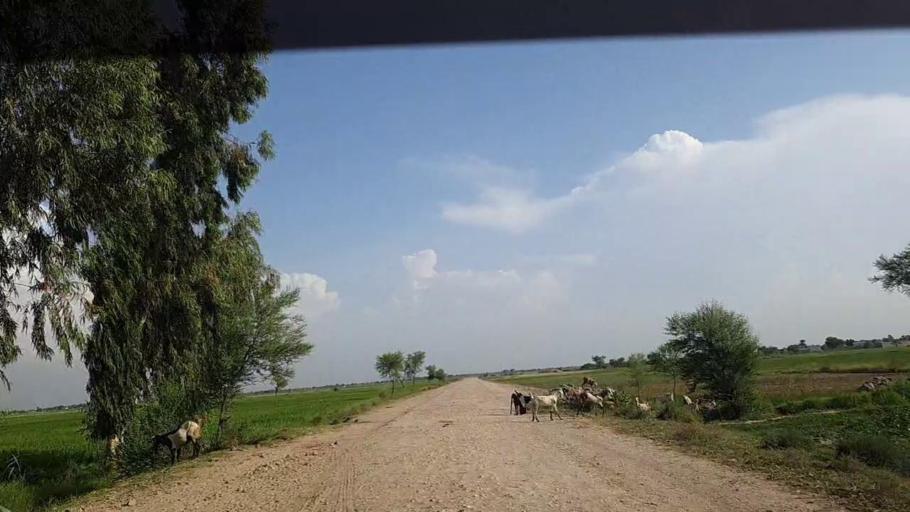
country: PK
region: Sindh
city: Khanpur
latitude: 27.8634
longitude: 69.3748
